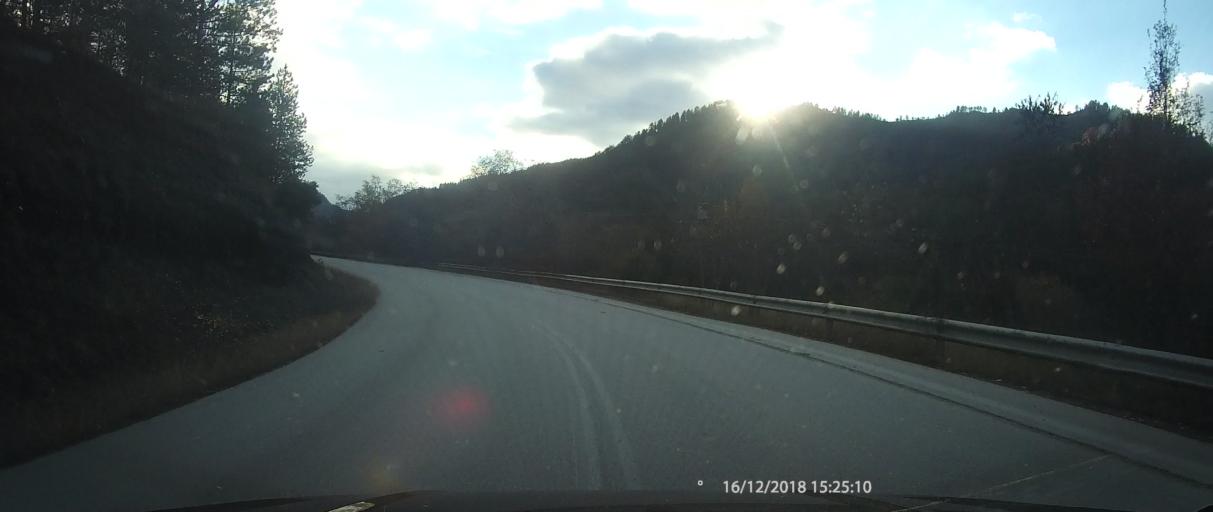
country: GR
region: Epirus
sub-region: Nomos Ioanninon
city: Konitsa
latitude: 40.1316
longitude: 20.7821
